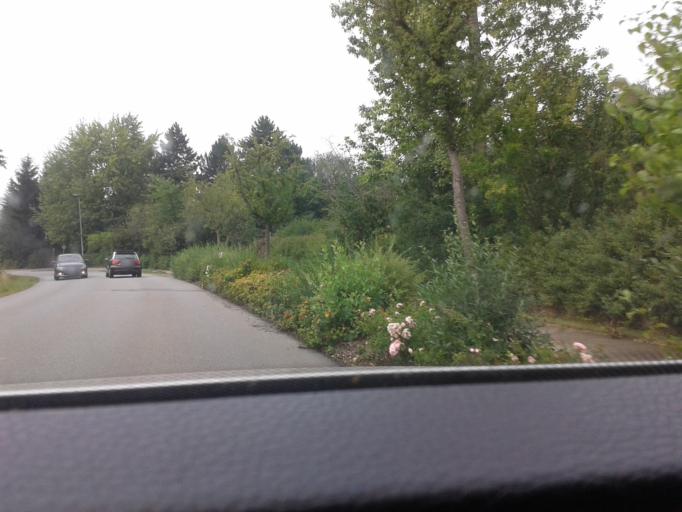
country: DE
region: Lower Saxony
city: Gifhorn
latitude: 52.4855
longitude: 10.5725
